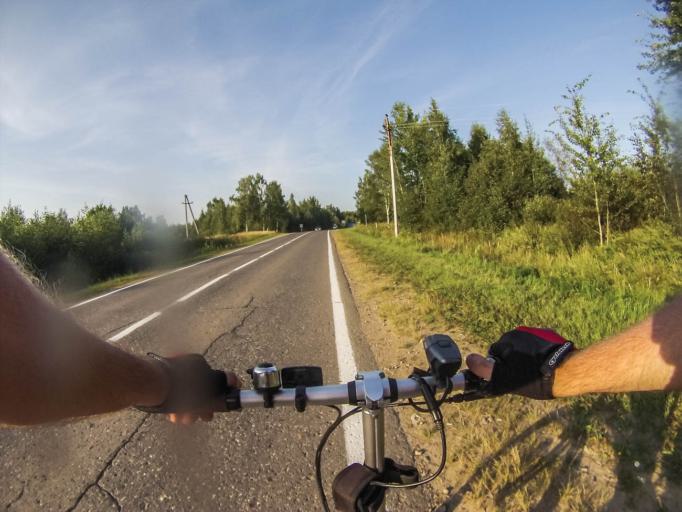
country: RU
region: Jaroslavl
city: Myshkin
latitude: 57.7543
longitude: 38.4397
